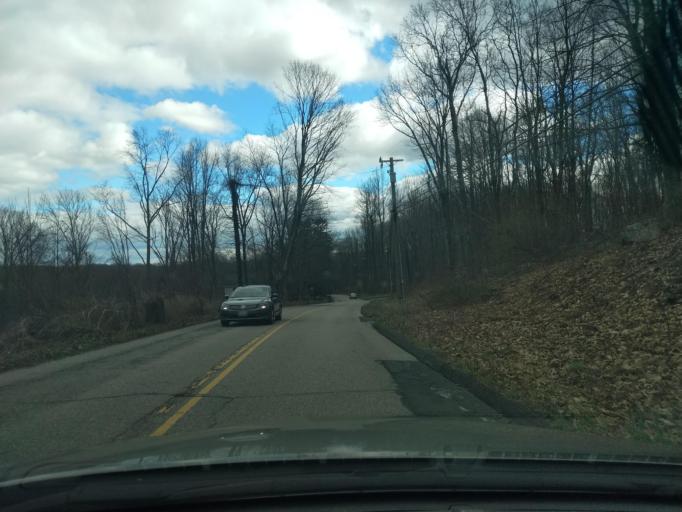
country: US
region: Connecticut
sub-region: Fairfield County
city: Newtown
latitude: 41.3587
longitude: -73.3248
